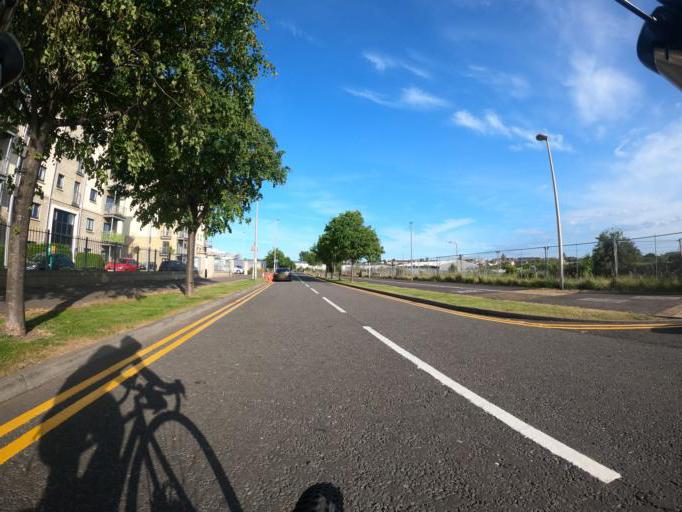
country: GB
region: Scotland
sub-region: Edinburgh
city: Edinburgh
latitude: 55.9844
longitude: -3.2296
